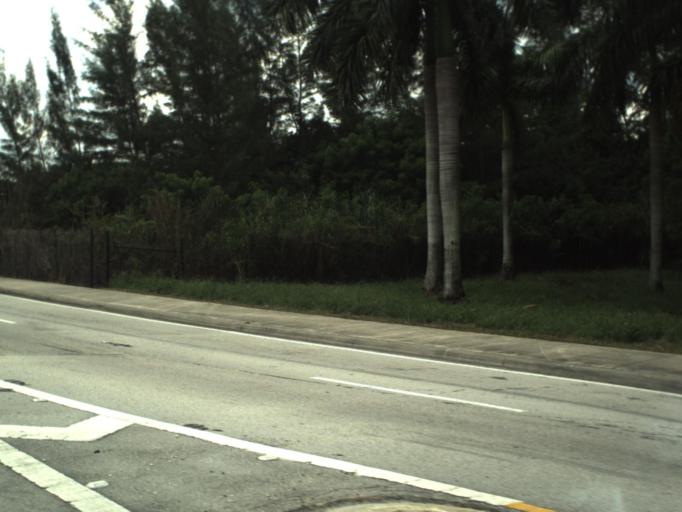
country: US
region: Florida
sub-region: Miami-Dade County
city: Tamiami
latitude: 25.7751
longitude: -80.4173
